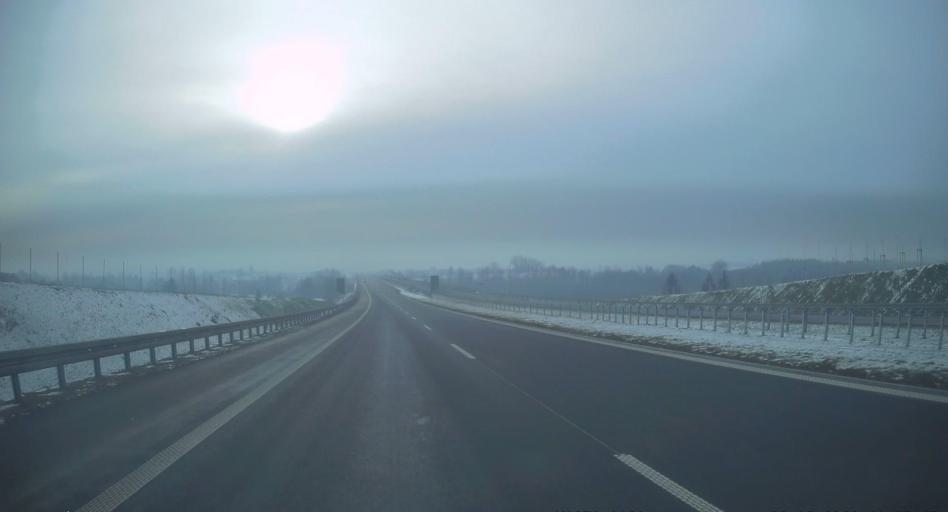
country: PL
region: Lesser Poland Voivodeship
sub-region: Powiat miechowski
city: Miechow
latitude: 50.3015
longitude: 20.0281
